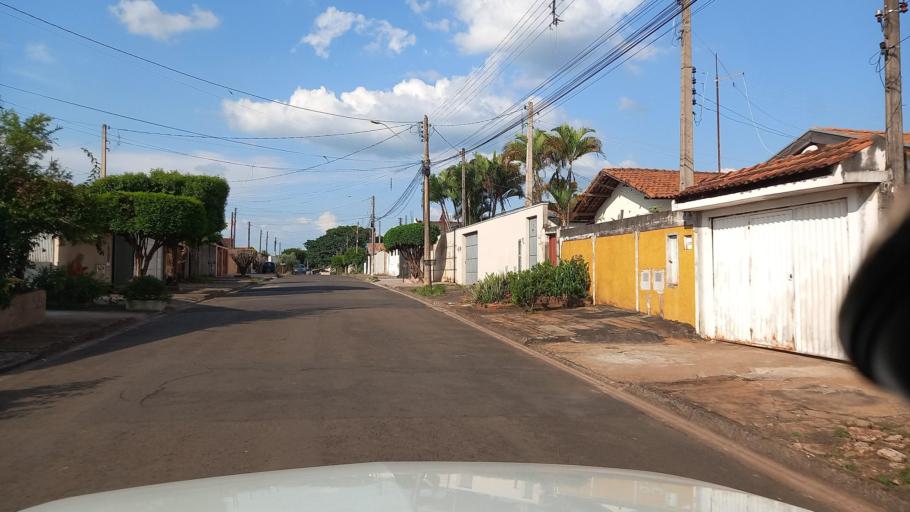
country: BR
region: Sao Paulo
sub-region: Moji-Guacu
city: Mogi-Gaucu
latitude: -22.3397
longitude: -46.9347
